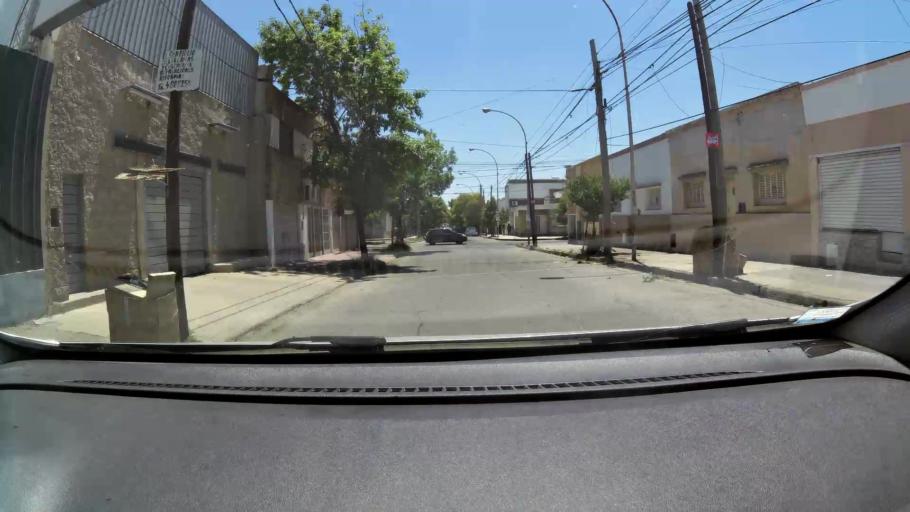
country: AR
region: Cordoba
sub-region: Departamento de Capital
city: Cordoba
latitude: -31.4092
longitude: -64.2145
